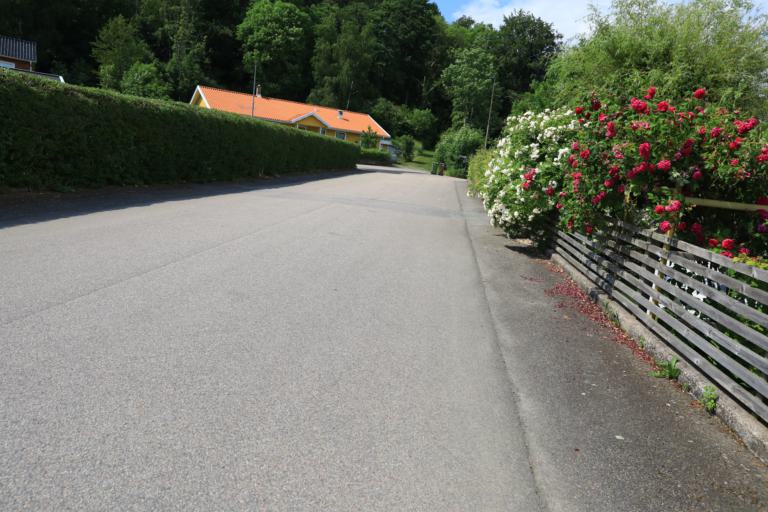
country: SE
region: Halland
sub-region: Varbergs Kommun
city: Varberg
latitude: 57.1702
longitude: 12.2968
